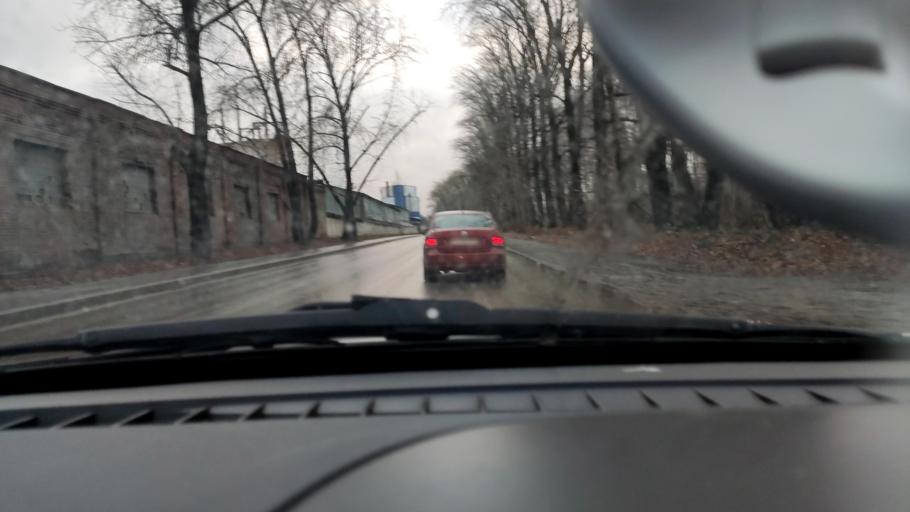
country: RU
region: Perm
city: Perm
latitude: 57.9598
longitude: 56.2073
